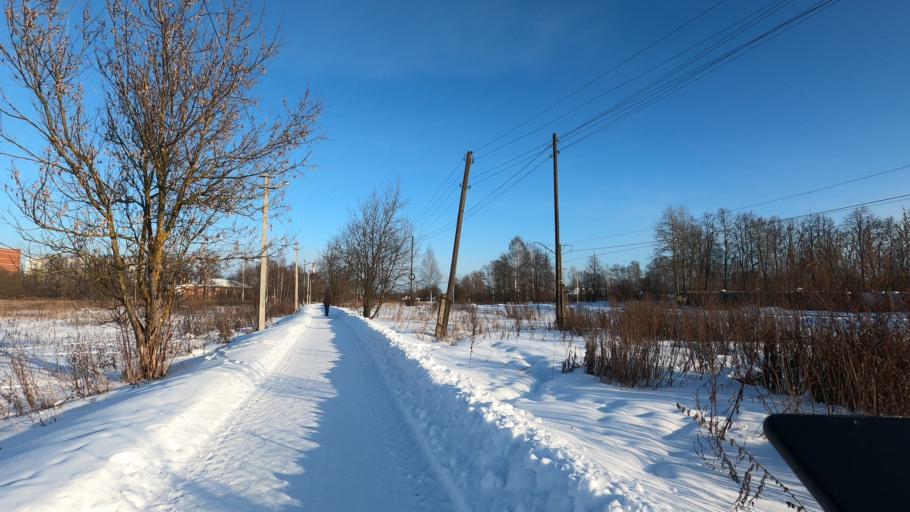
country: RU
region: Moskovskaya
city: Pavlovskiy Posad
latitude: 55.7748
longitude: 38.7043
